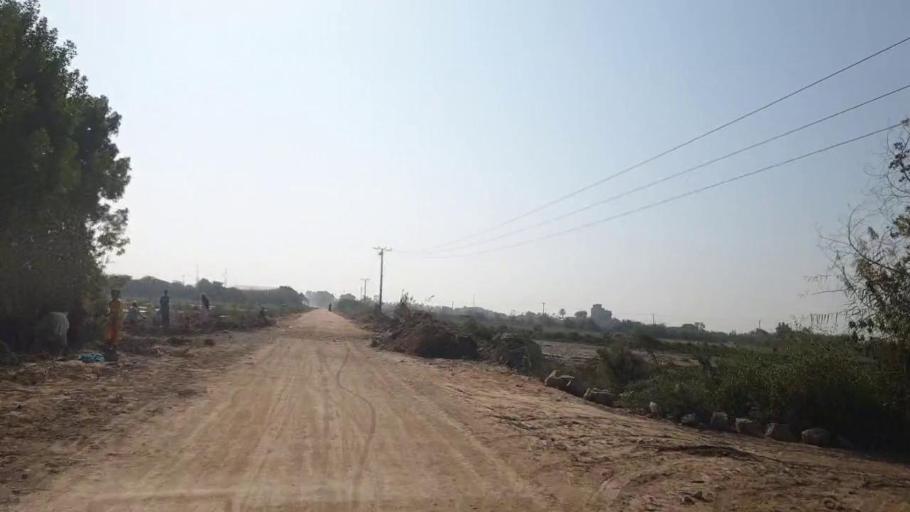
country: PK
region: Sindh
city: Thatta
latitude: 24.7625
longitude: 67.9151
